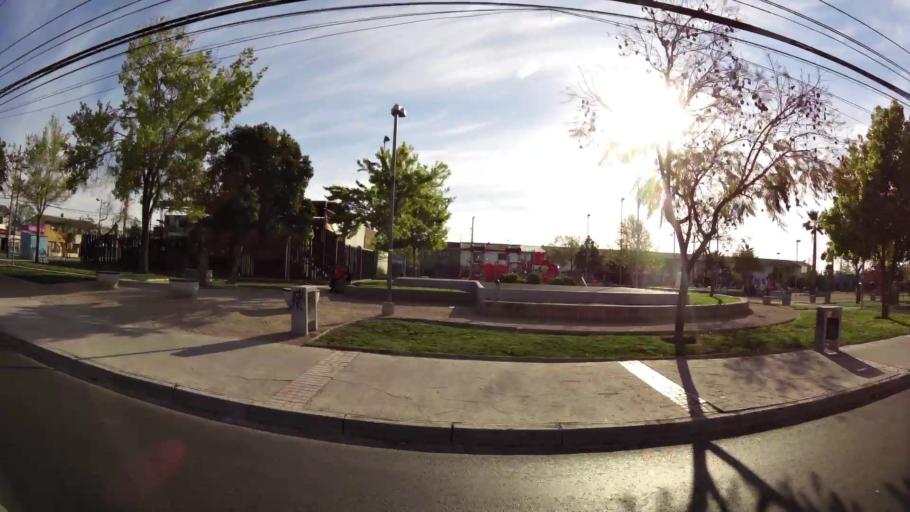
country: CL
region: Santiago Metropolitan
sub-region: Provincia de Cordillera
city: Puente Alto
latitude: -33.6158
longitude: -70.5748
